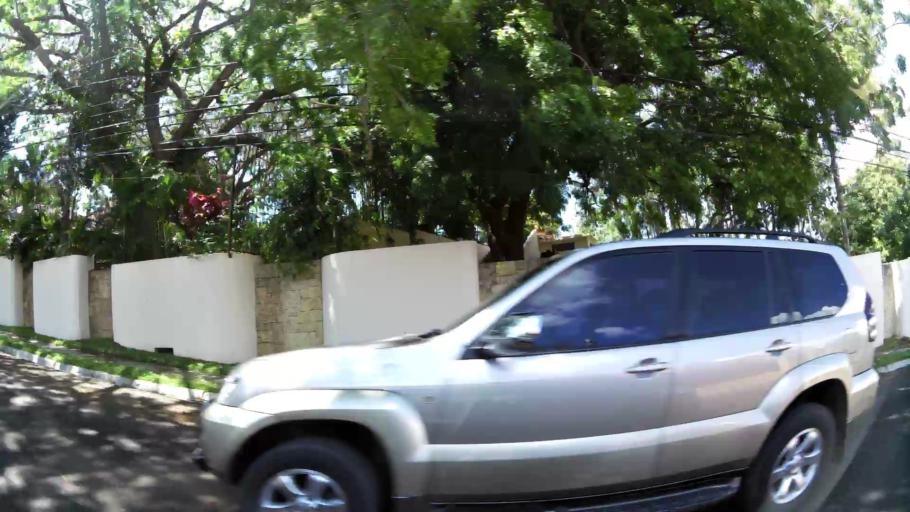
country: DO
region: Santiago
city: Santiago de los Caballeros
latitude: 19.4677
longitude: -70.6783
